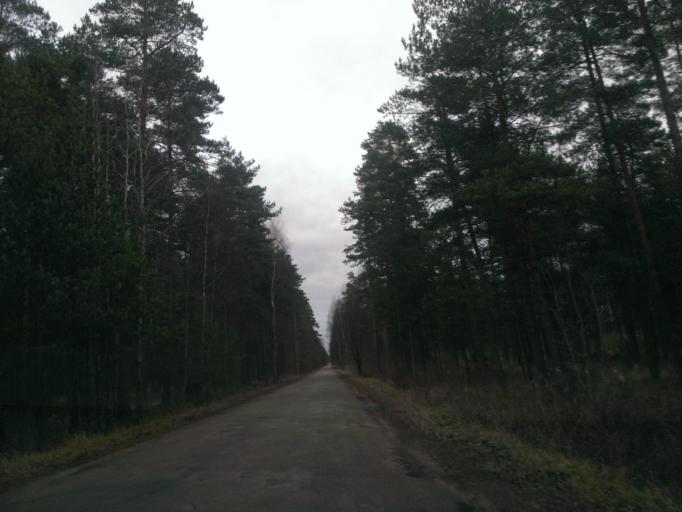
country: LV
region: Riga
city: Bergi
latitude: 57.0024
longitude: 24.3081
